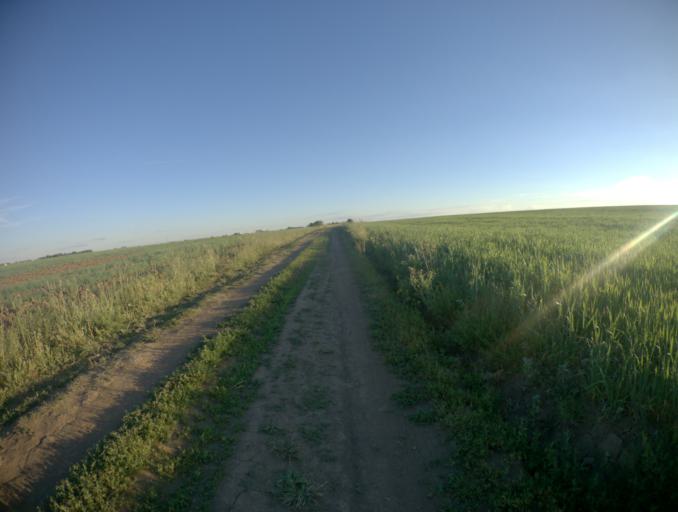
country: RU
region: Vladimir
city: Bogolyubovo
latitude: 56.2041
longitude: 40.5066
